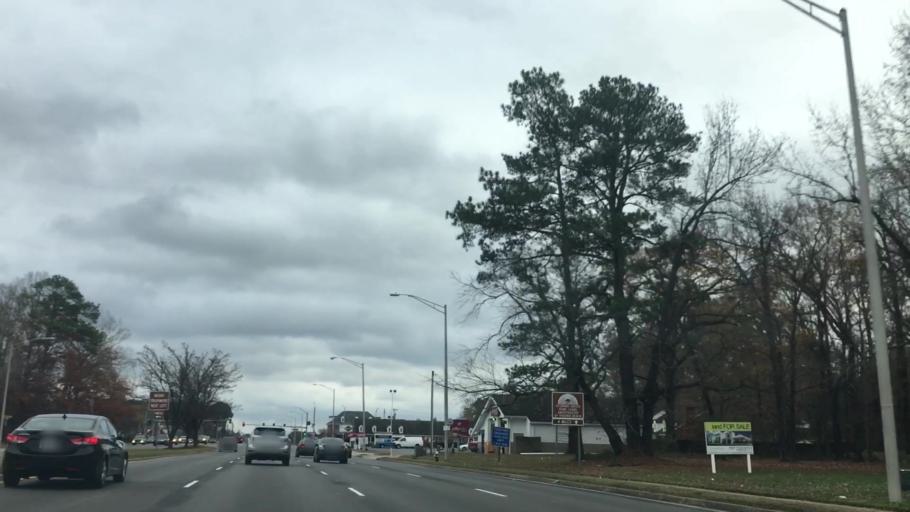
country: US
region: Virginia
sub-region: City of Chesapeake
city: Chesapeake
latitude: 36.8277
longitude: -76.1334
